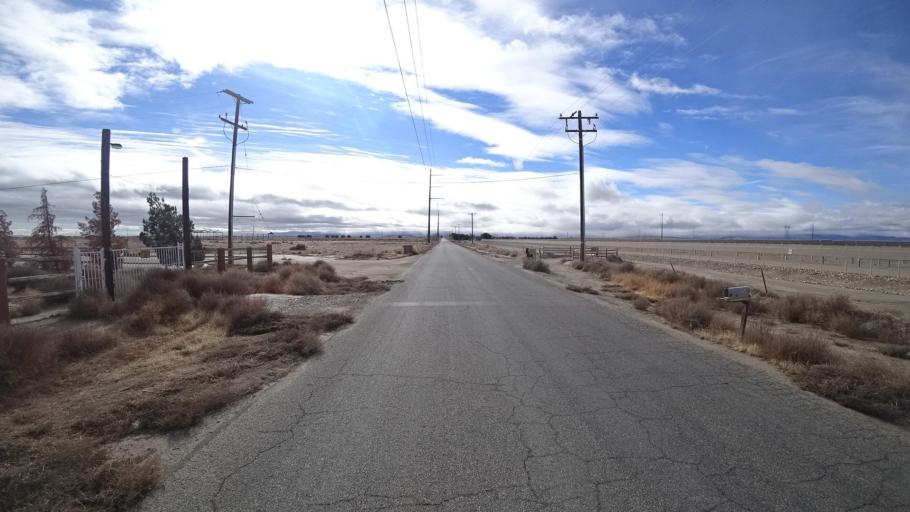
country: US
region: California
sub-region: Kern County
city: Rosamond
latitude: 34.8382
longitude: -118.3086
